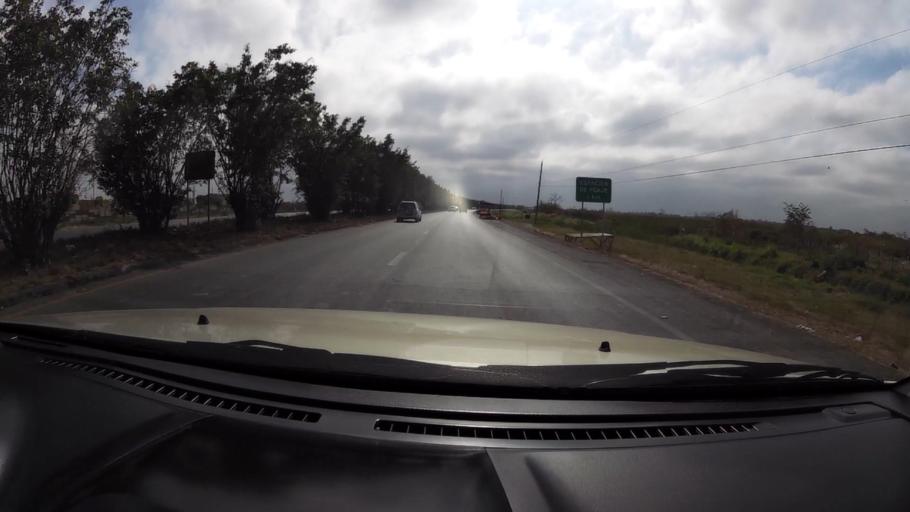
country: EC
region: Guayas
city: Eloy Alfaro
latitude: -2.1996
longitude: -79.7627
